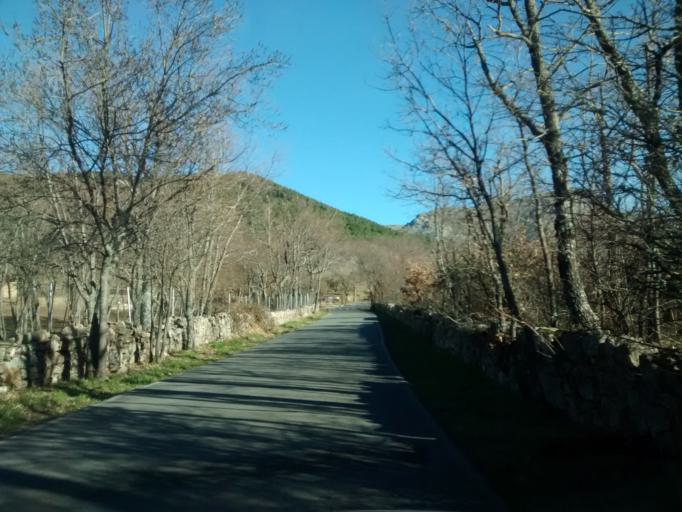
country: ES
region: Madrid
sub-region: Provincia de Madrid
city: Navacerrada
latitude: 40.7372
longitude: -4.0094
